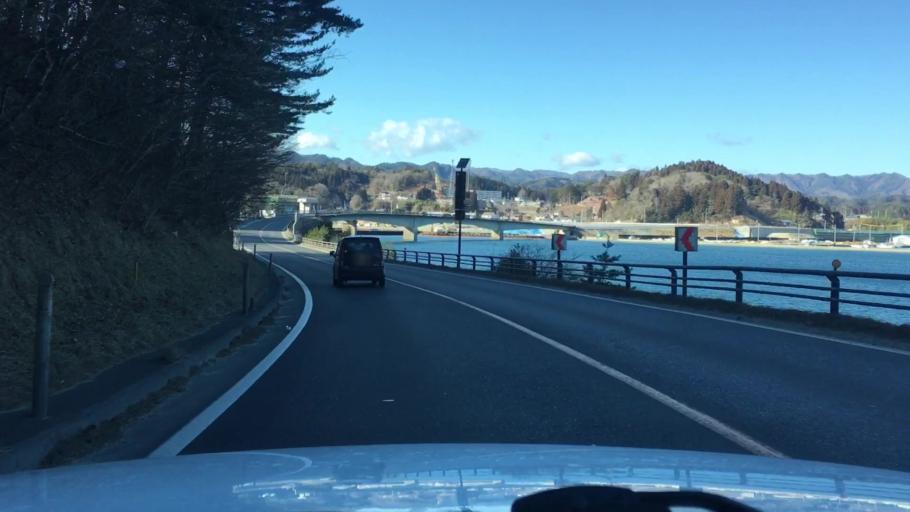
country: JP
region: Iwate
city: Yamada
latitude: 39.4475
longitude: 141.9670
